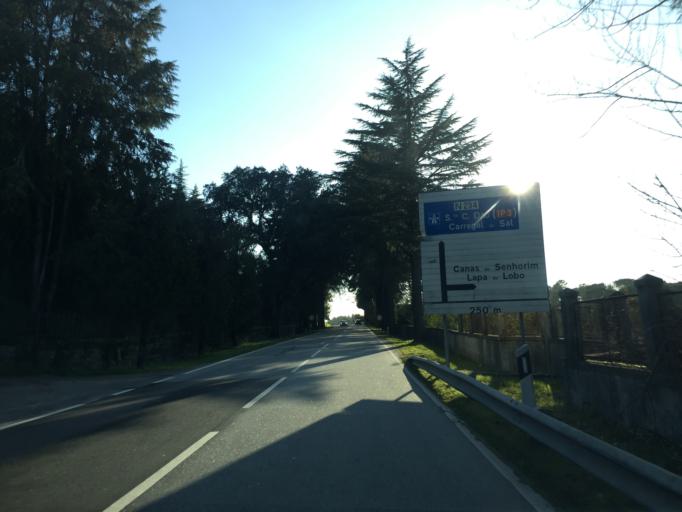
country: PT
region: Viseu
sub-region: Nelas
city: Nelas
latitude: 40.4890
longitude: -7.9065
